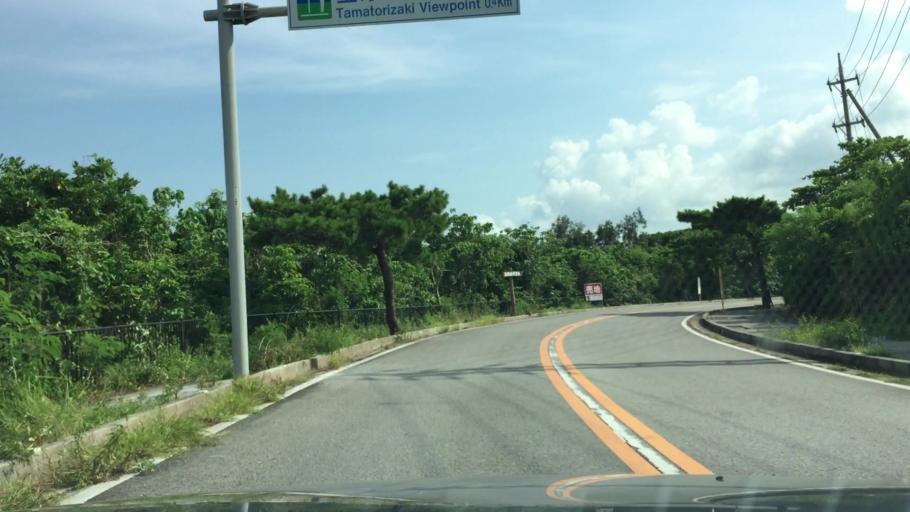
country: JP
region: Okinawa
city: Ishigaki
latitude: 24.4901
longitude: 124.2799
